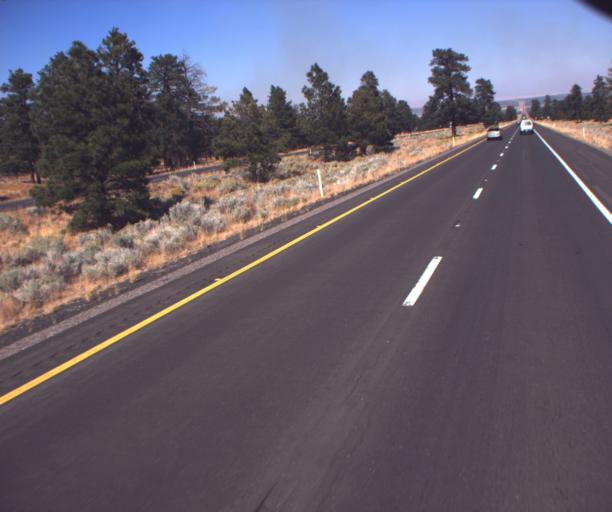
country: US
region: Arizona
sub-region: Coconino County
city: Flagstaff
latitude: 35.3871
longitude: -111.5793
